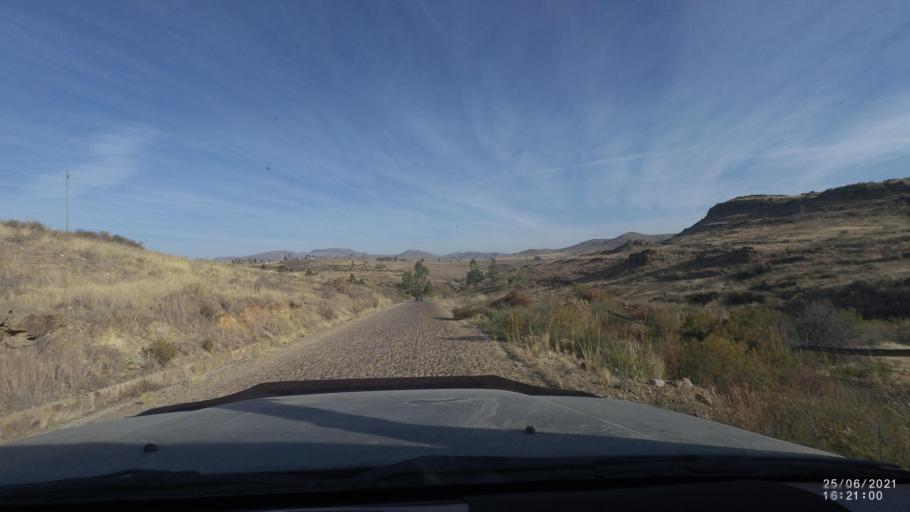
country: BO
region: Cochabamba
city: Cliza
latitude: -17.7493
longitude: -65.8388
